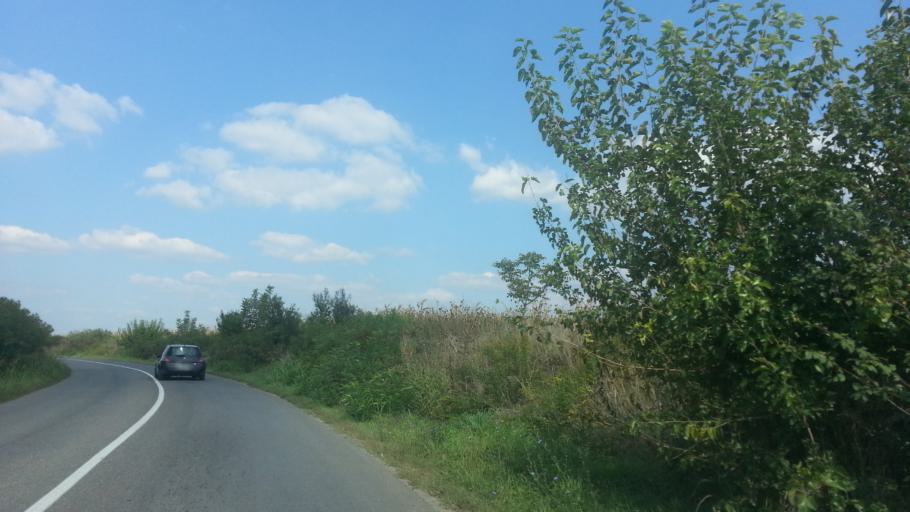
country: RS
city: Novi Banovci
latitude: 44.9217
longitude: 20.2814
